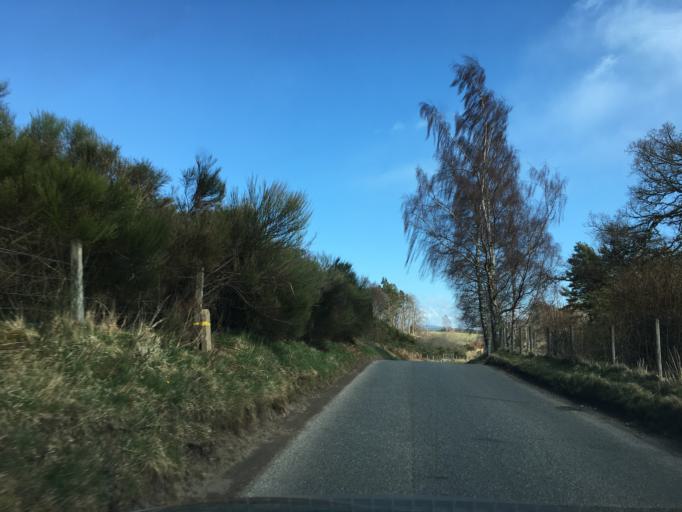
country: GB
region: Scotland
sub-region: Highland
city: Aviemore
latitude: 57.2049
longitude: -3.7898
